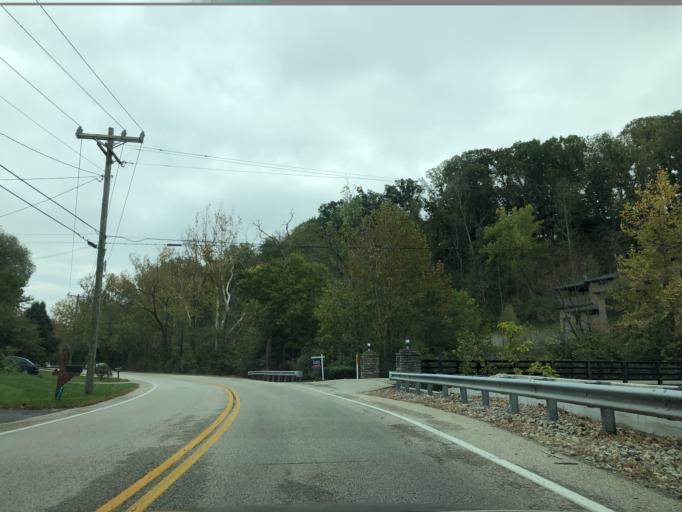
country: US
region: Ohio
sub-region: Hamilton County
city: The Village of Indian Hill
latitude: 39.2528
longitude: -84.3022
